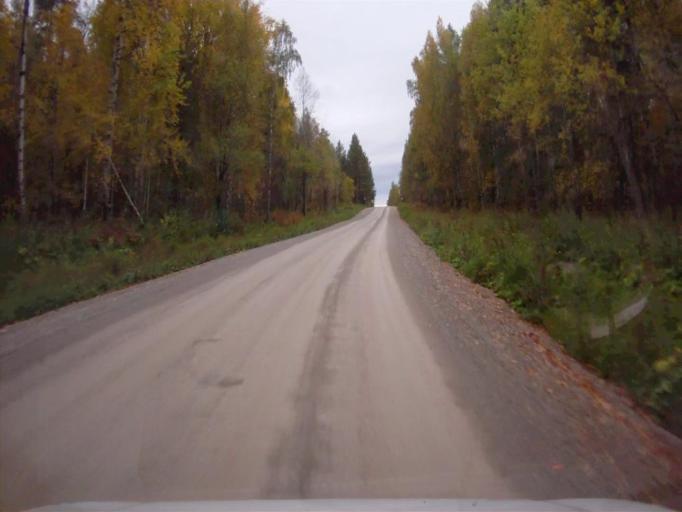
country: RU
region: Chelyabinsk
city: Nyazepetrovsk
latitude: 56.0692
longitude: 59.4323
